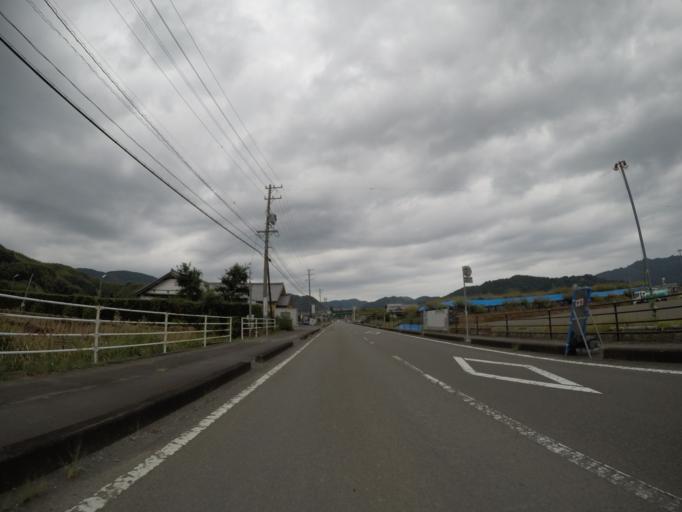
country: JP
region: Shizuoka
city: Fujieda
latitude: 34.9072
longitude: 138.2623
